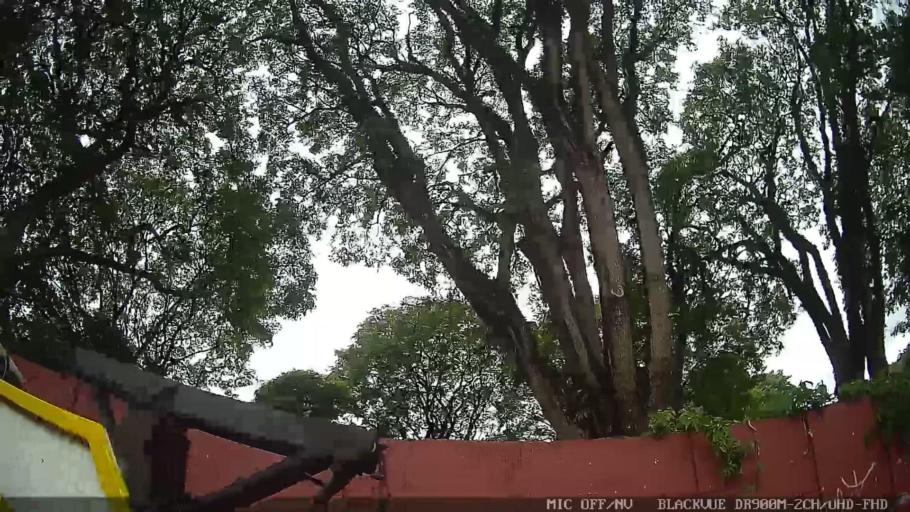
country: BR
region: Sao Paulo
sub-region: Sao Paulo
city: Sao Paulo
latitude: -23.5100
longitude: -46.6723
